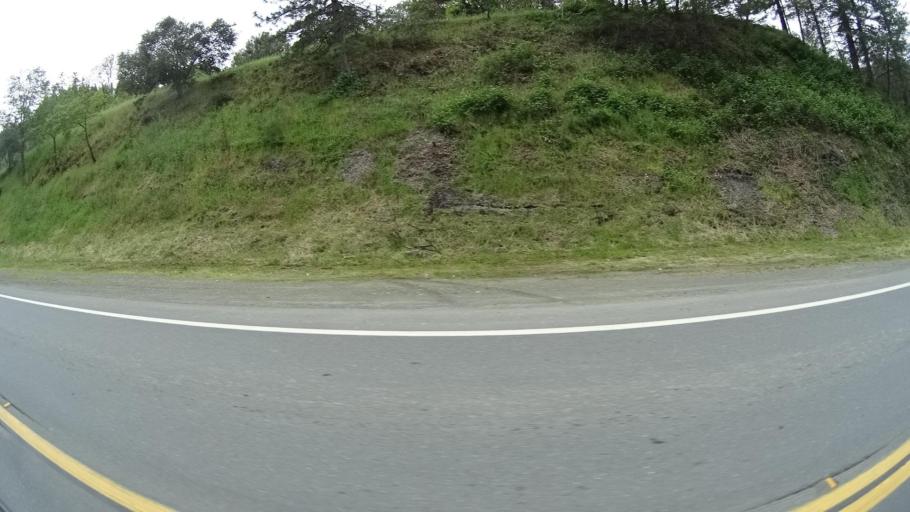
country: US
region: California
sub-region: Humboldt County
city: Willow Creek
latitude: 40.9420
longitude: -123.6324
